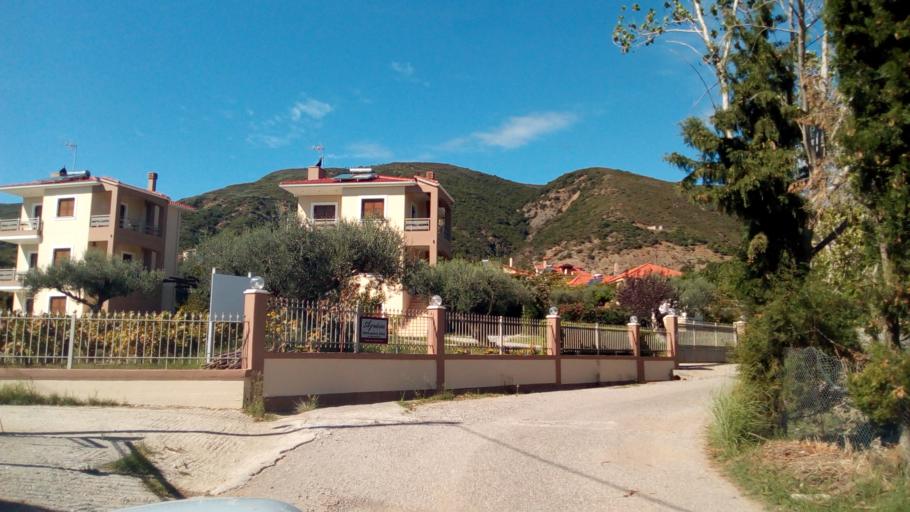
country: GR
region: West Greece
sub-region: Nomos Aitolias kai Akarnanias
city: Antirrio
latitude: 38.3716
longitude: 21.7748
